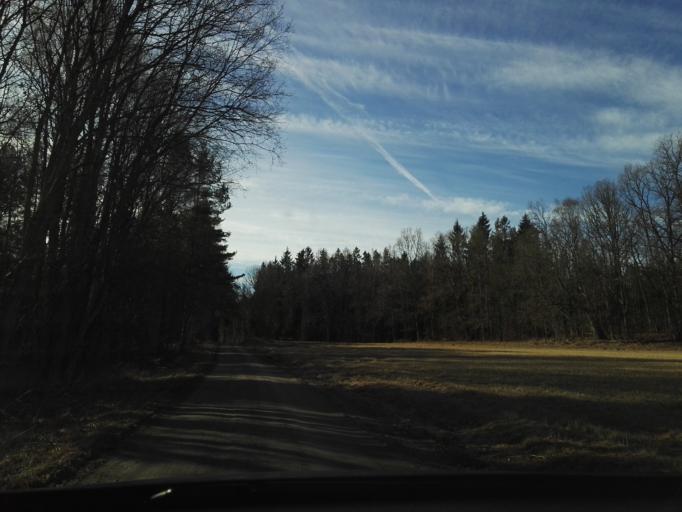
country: SE
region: Kronoberg
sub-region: Vaxjo Kommun
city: Vaexjoe
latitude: 56.9258
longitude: 14.7496
